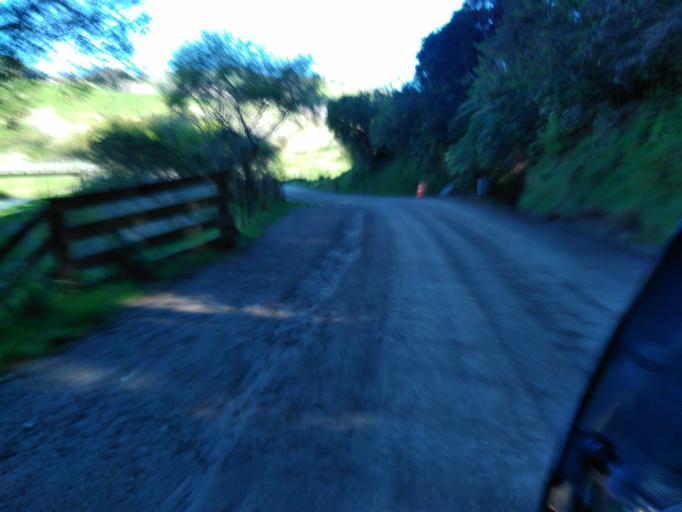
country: NZ
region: Gisborne
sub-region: Gisborne District
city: Gisborne
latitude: -38.3750
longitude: 177.6126
